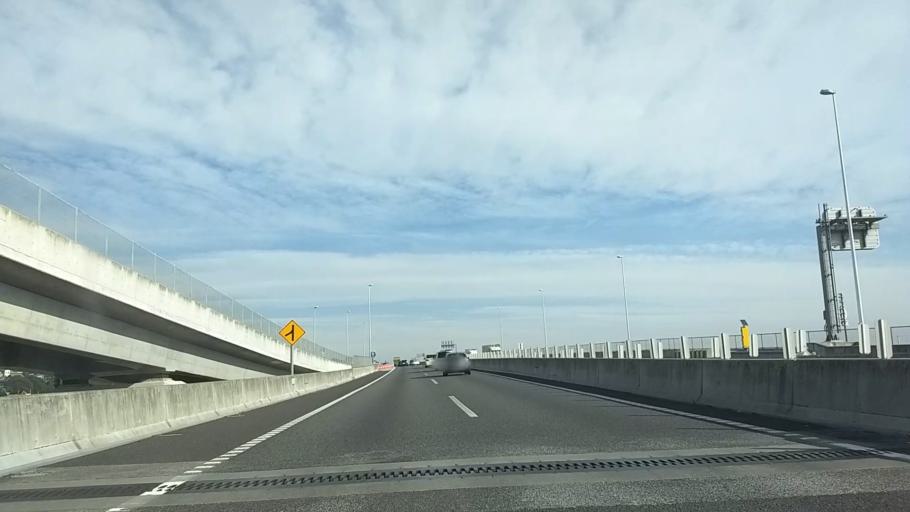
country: JP
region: Kanagawa
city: Zama
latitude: 35.4813
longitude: 139.3723
